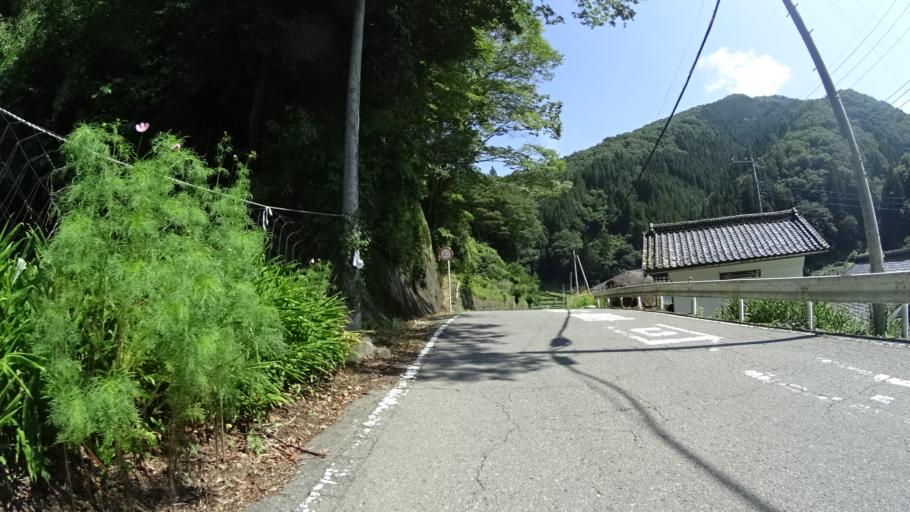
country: JP
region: Gunma
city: Tomioka
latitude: 36.0624
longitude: 138.8318
